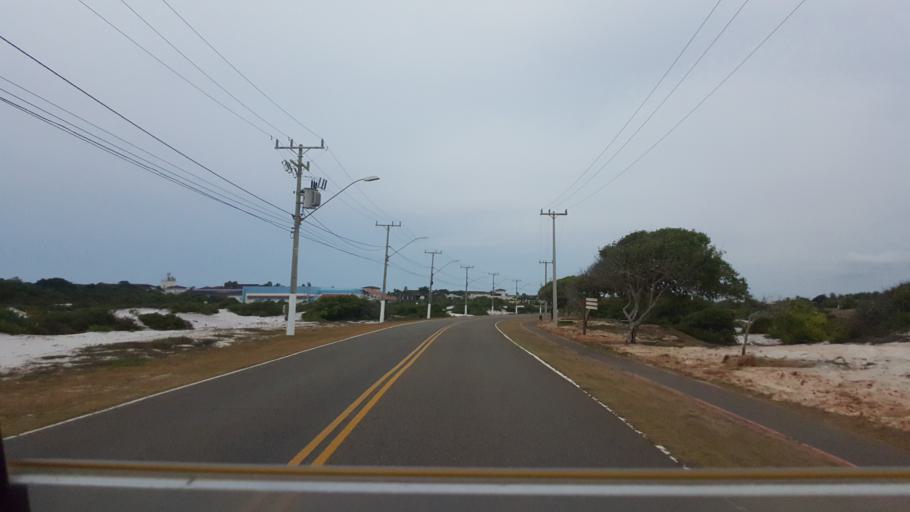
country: BR
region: Bahia
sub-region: Mata De Sao Joao
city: Mata de Sao Joao
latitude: -12.4336
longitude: -37.9200
